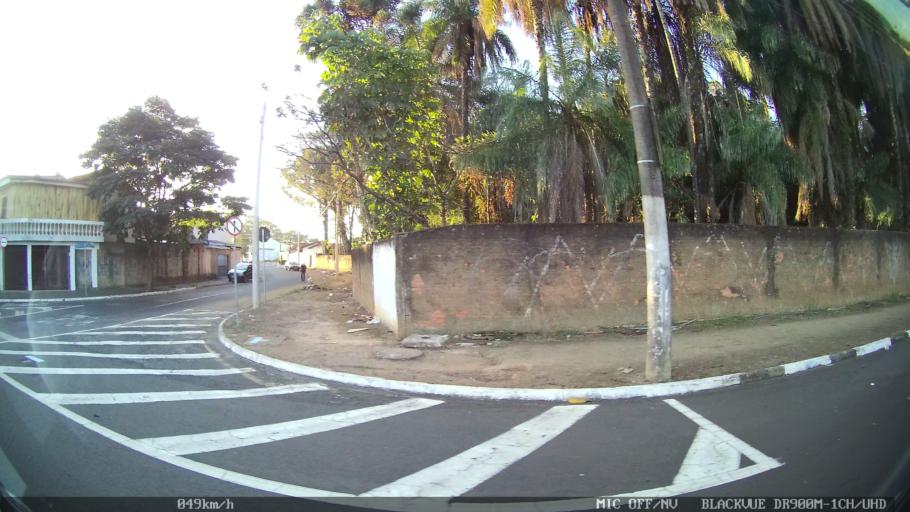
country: BR
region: Sao Paulo
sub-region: Franca
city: Franca
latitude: -20.4929
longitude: -47.4003
